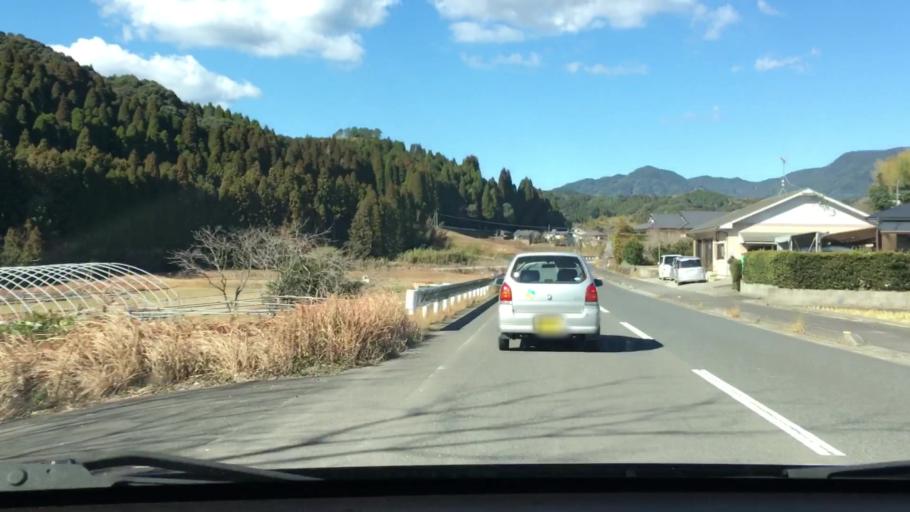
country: JP
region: Kagoshima
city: Ijuin
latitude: 31.6927
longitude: 130.4630
